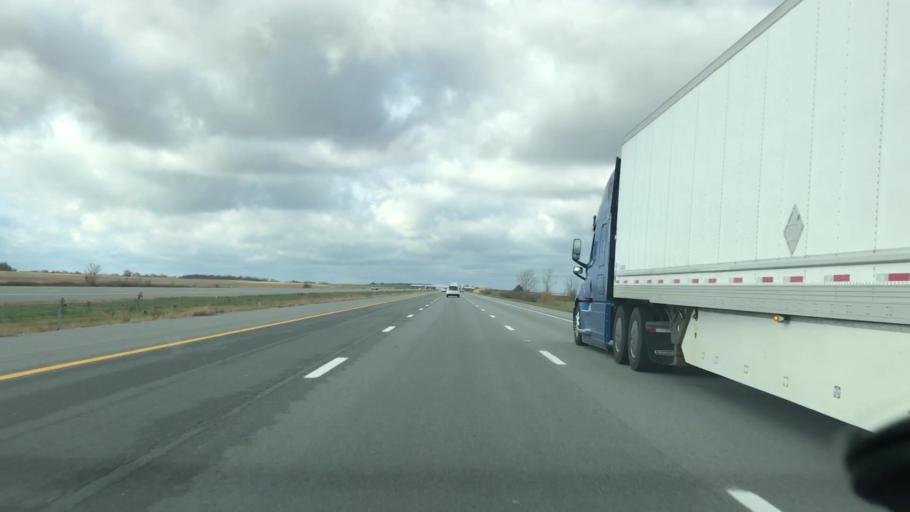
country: US
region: Ohio
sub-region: Madison County
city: Choctaw Lake
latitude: 39.9421
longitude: -83.4580
